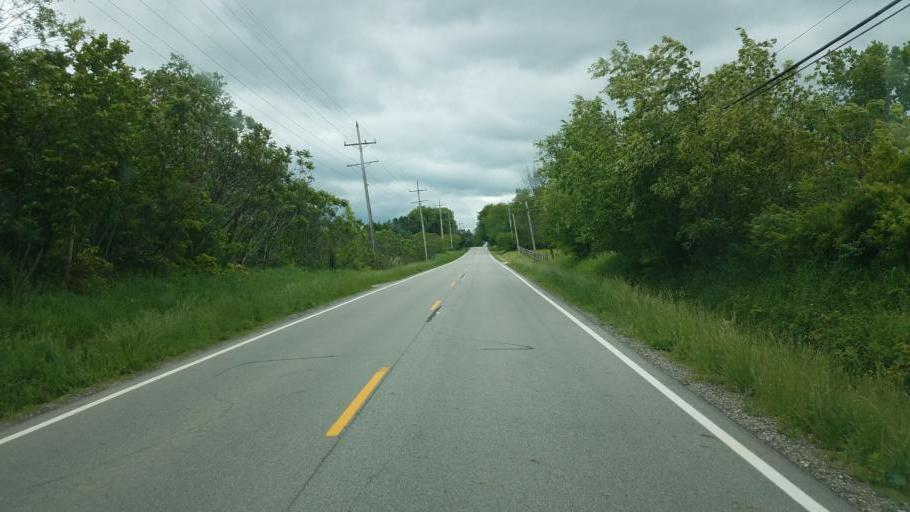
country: US
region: Ohio
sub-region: Geauga County
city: Burton
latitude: 41.3962
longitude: -81.1717
